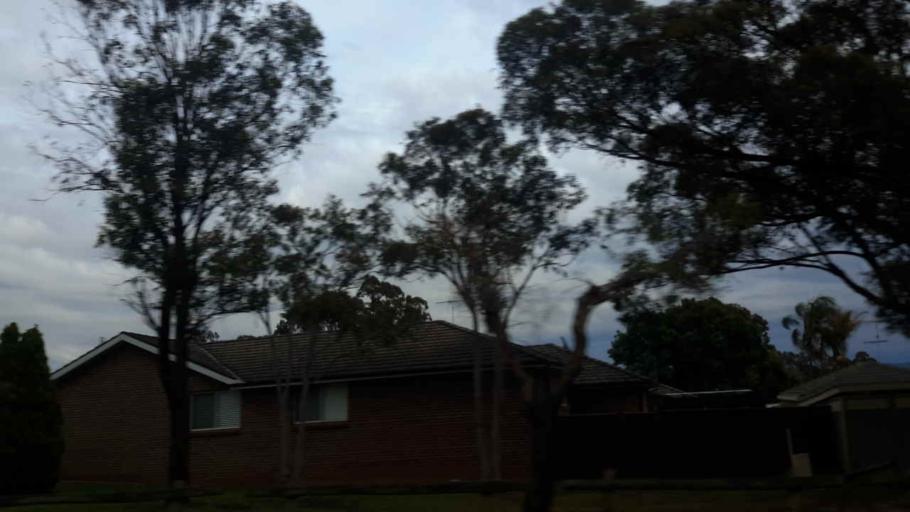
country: AU
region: New South Wales
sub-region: Camden
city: Camden South
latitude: -34.0852
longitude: 150.6949
